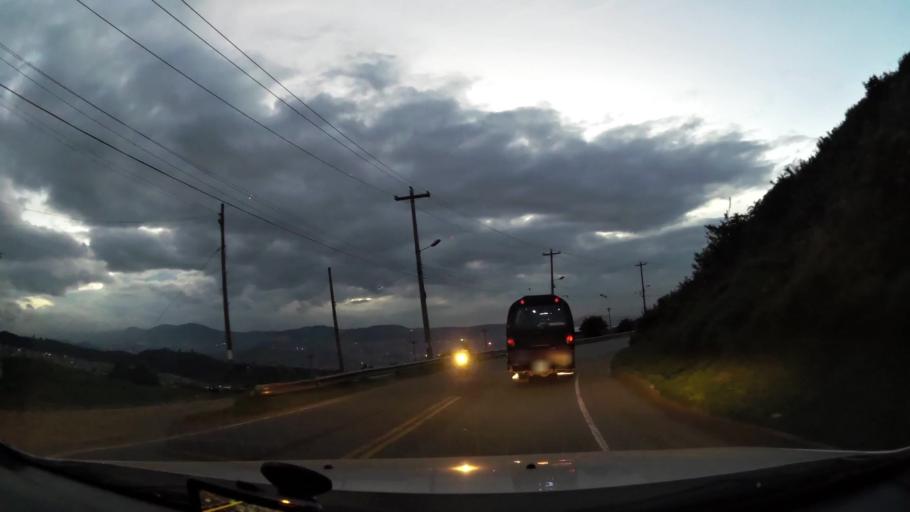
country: CO
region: Bogota D.C.
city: Bogota
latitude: 4.5491
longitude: -74.0858
